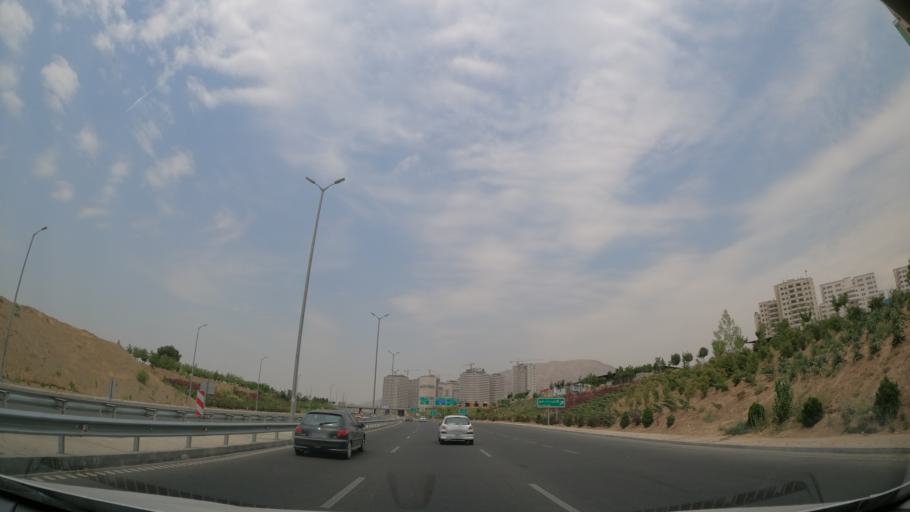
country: IR
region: Tehran
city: Shahr-e Qods
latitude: 35.7448
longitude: 51.1952
